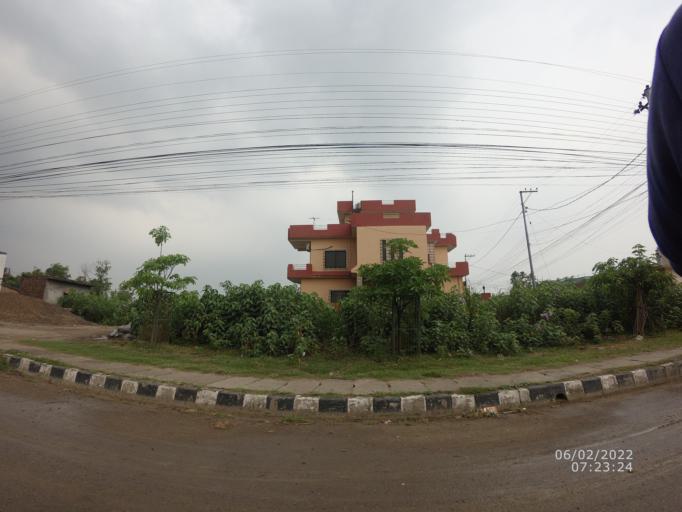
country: NP
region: Western Region
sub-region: Lumbini Zone
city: Bhairahawa
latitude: 27.4949
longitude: 83.4463
